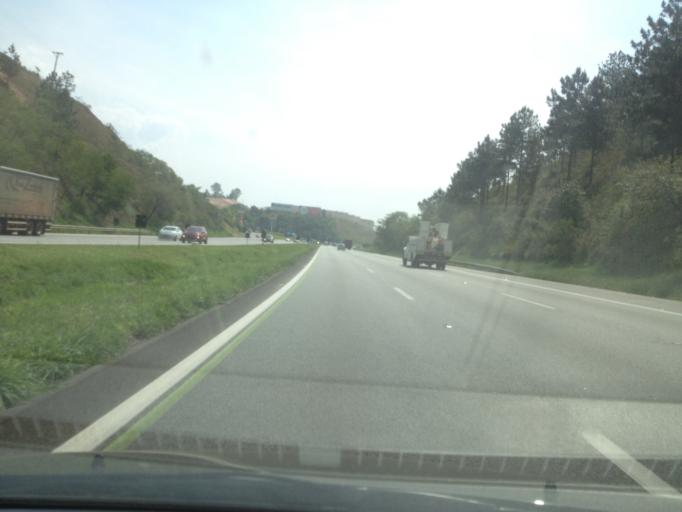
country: BR
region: Sao Paulo
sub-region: Sao Roque
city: Sao Roque
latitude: -23.4287
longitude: -47.1340
